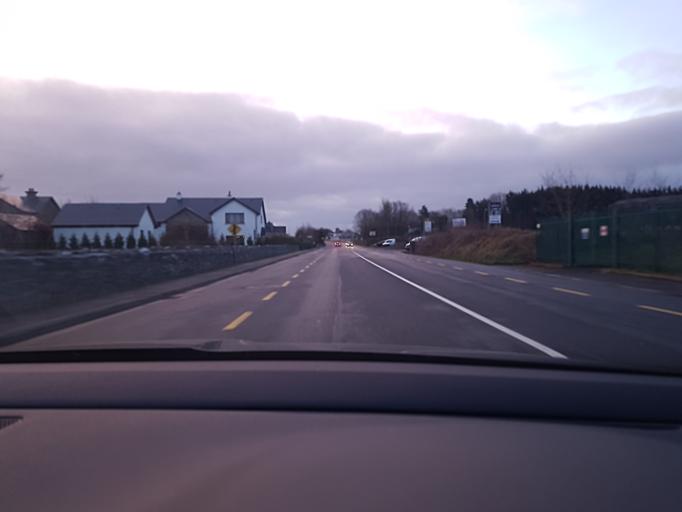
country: IE
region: Connaught
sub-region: County Galway
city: Tuam
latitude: 53.5293
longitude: -8.8740
